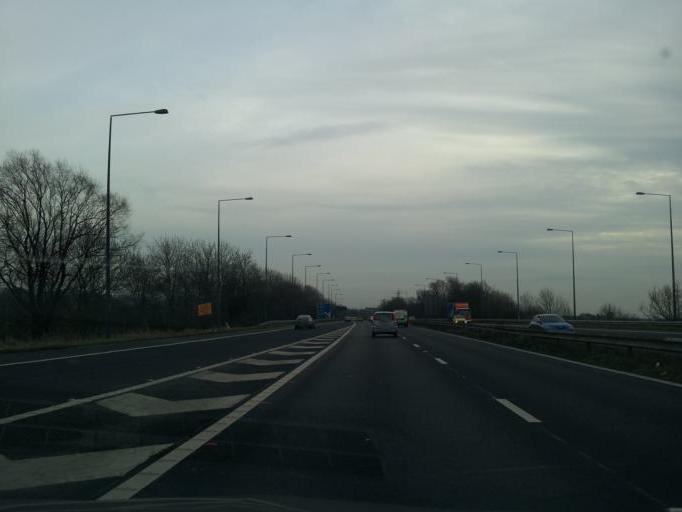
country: GB
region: England
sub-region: Borough of Oldham
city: Royton
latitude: 53.5712
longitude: -2.1588
